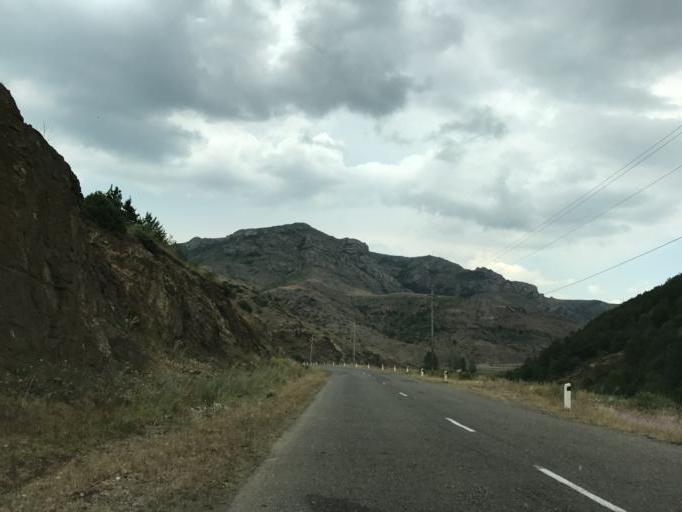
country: AZ
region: Susa
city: Shushi
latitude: 39.7143
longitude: 46.6627
